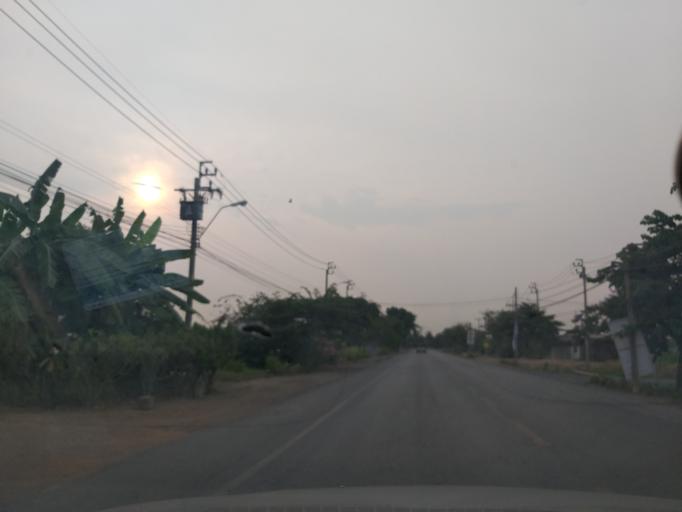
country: TH
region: Bangkok
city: Nong Chok
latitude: 13.8255
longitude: 100.9185
